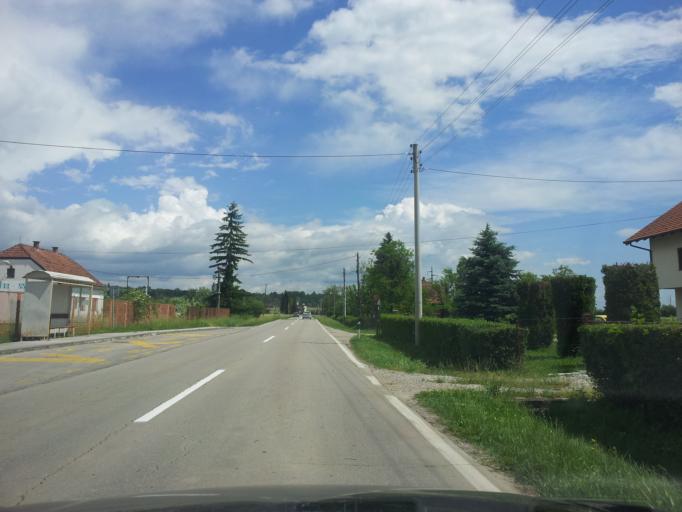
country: HR
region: Karlovacka
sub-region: Grad Karlovac
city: Karlovac
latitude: 45.5585
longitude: 15.5780
